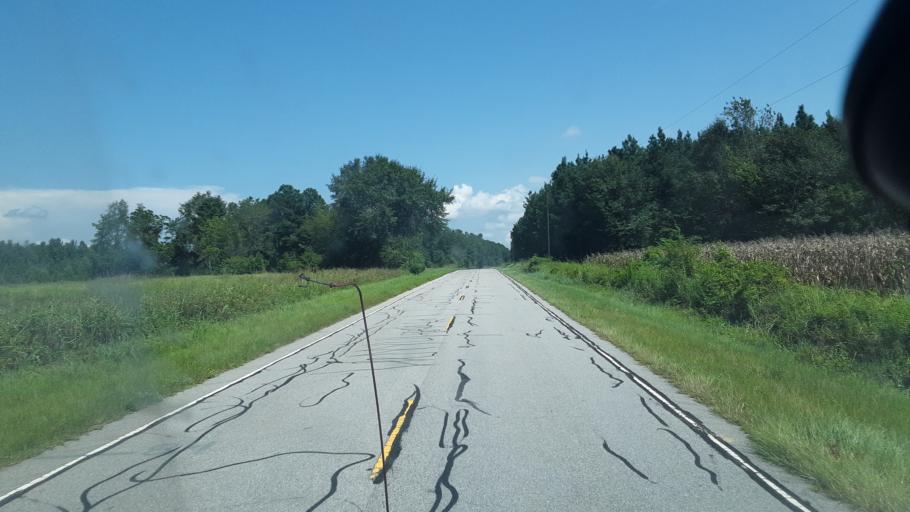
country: US
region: South Carolina
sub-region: Orangeburg County
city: Edisto
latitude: 33.5924
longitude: -81.0299
